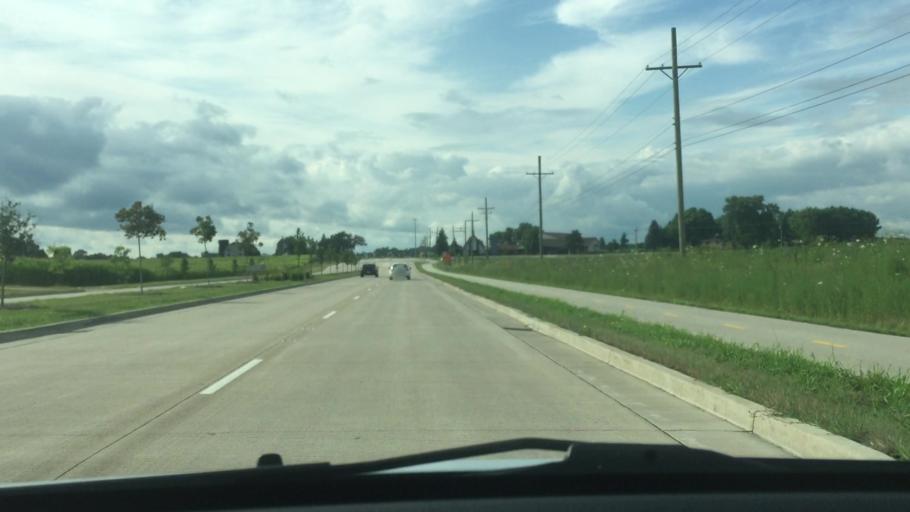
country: US
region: Illinois
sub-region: McHenry County
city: Lakewood
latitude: 42.2648
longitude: -88.3762
